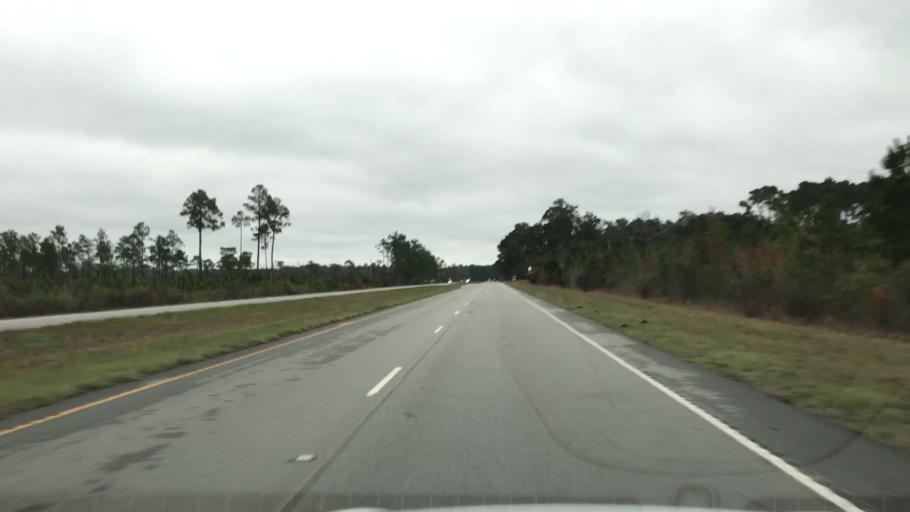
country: US
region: South Carolina
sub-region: Charleston County
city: Awendaw
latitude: 33.1714
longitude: -79.4188
